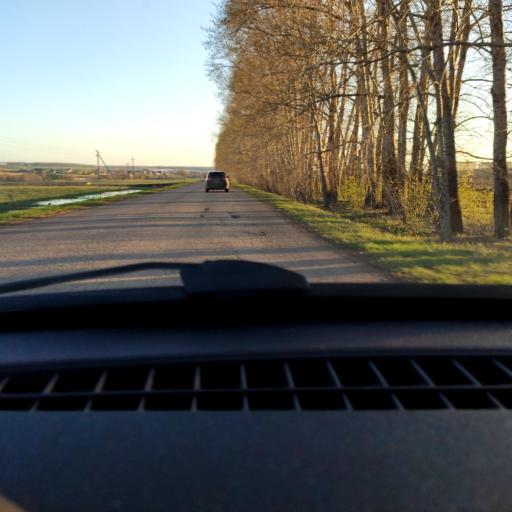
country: RU
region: Bashkortostan
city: Avdon
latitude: 54.4963
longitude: 55.6133
